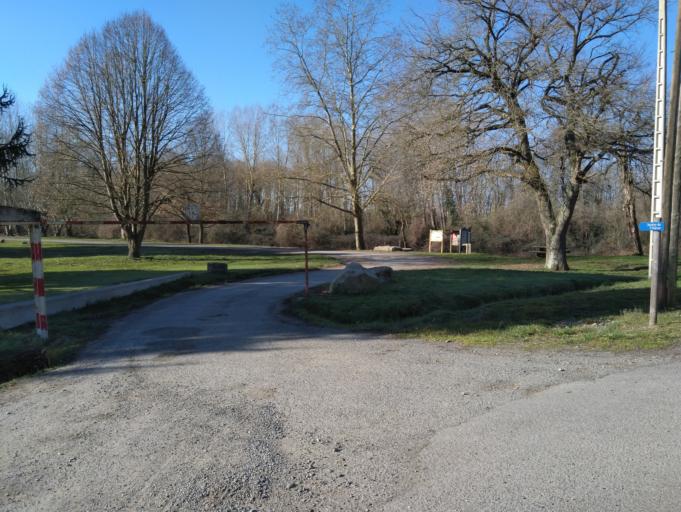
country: FR
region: Midi-Pyrenees
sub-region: Departement des Hautes-Pyrenees
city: Andrest
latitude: 43.3574
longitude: 0.0921
